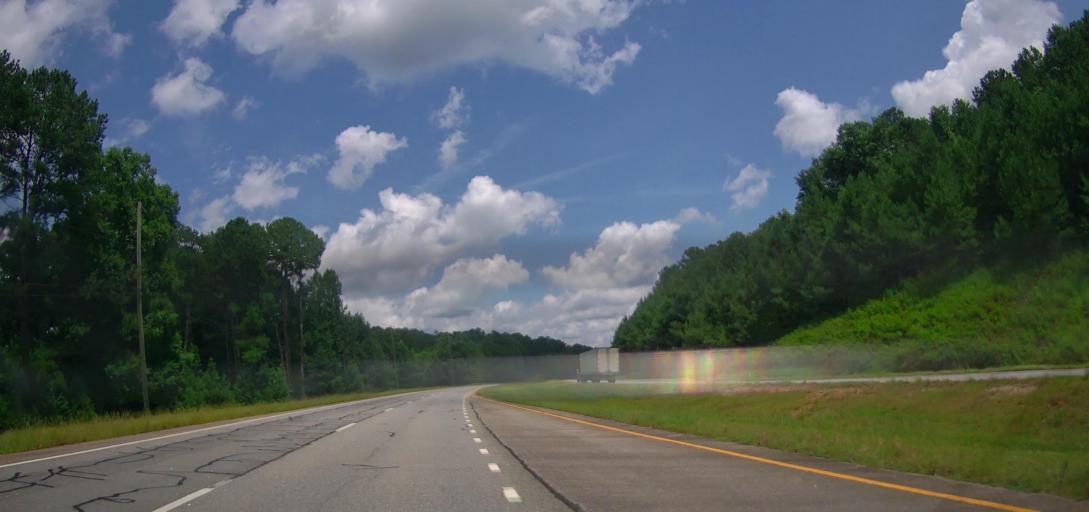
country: US
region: Georgia
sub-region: Heard County
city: Franklin
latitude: 33.2580
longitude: -85.0572
